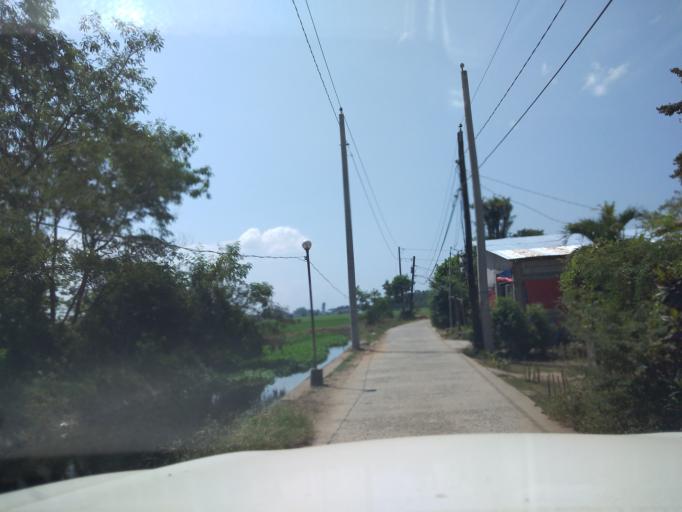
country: PH
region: Central Luzon
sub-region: Province of Pampanga
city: Talang
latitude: 15.0242
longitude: 120.8382
